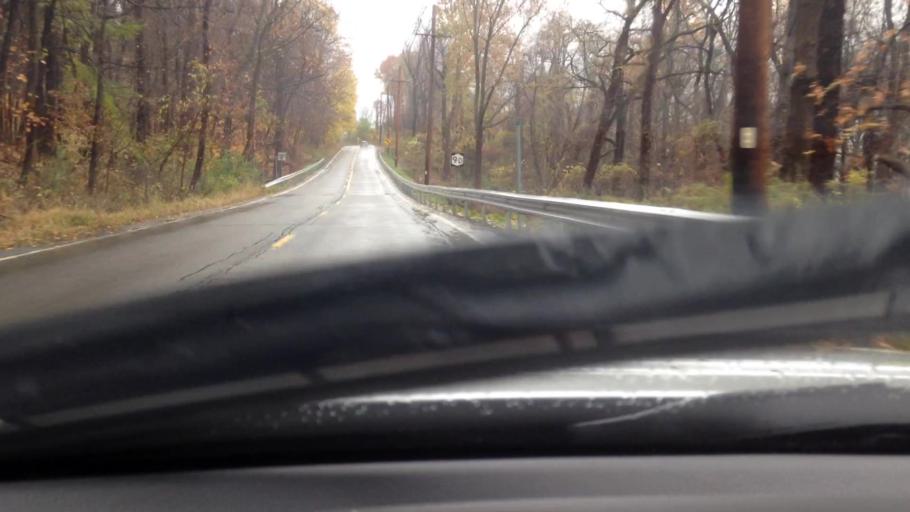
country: US
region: New York
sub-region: Orange County
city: Cornwall-on-Hudson
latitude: 41.4540
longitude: -73.9822
